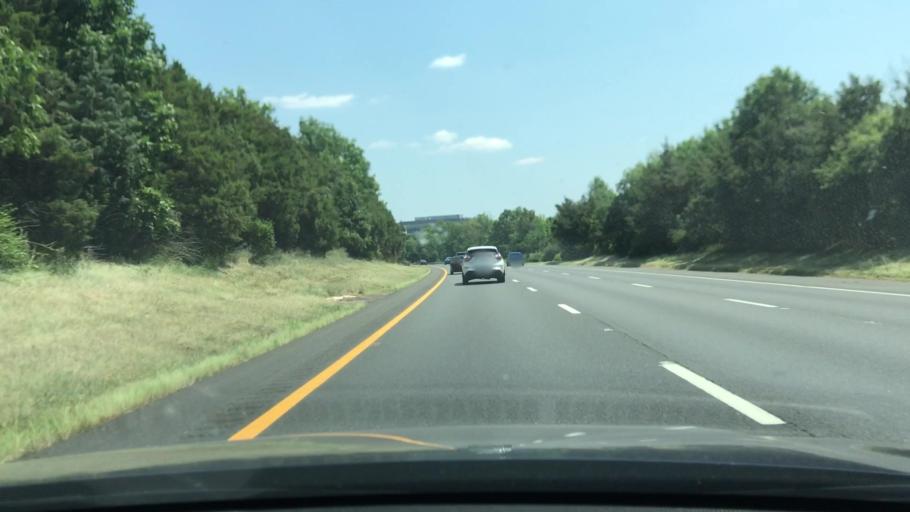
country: US
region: New Jersey
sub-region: Somerset County
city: Green Knoll
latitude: 40.5897
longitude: -74.6188
